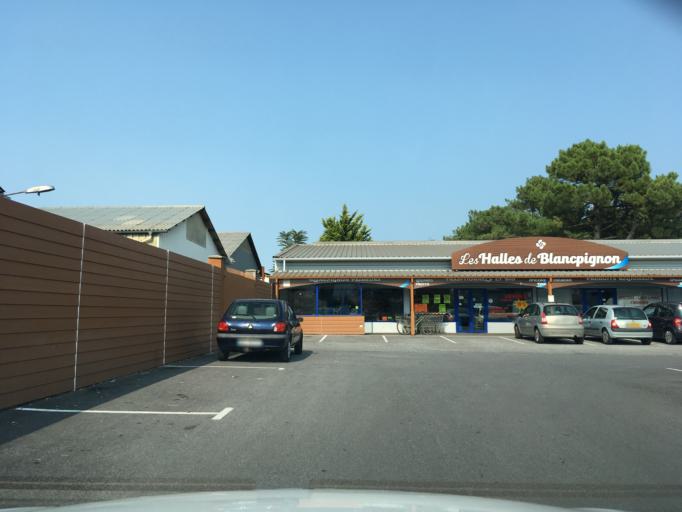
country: FR
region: Aquitaine
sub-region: Departement des Pyrenees-Atlantiques
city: Boucau
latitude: 43.5209
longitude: -1.5020
